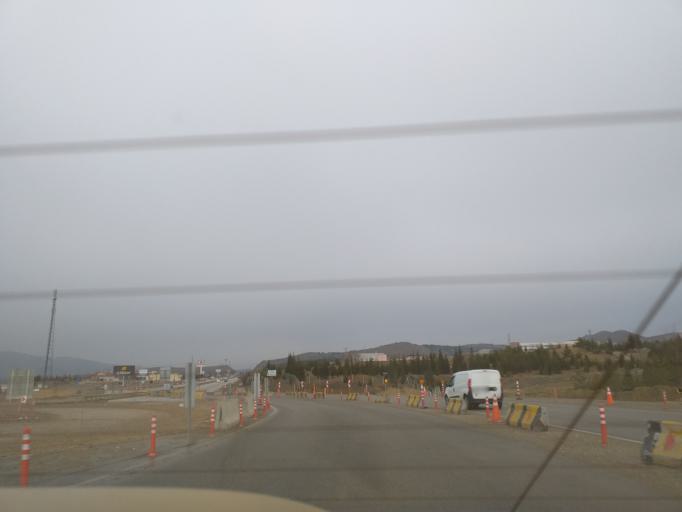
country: TR
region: Kirikkale
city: Yahsihan
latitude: 39.8764
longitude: 33.4425
